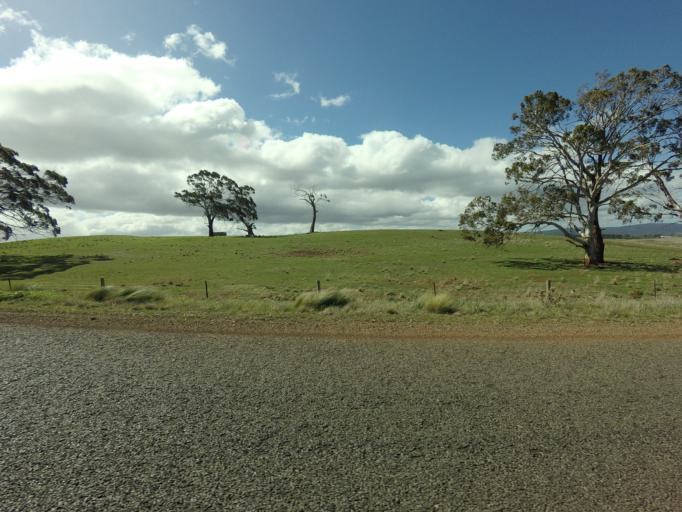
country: AU
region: Tasmania
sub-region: Northern Midlands
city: Evandale
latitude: -41.9091
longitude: 147.4596
